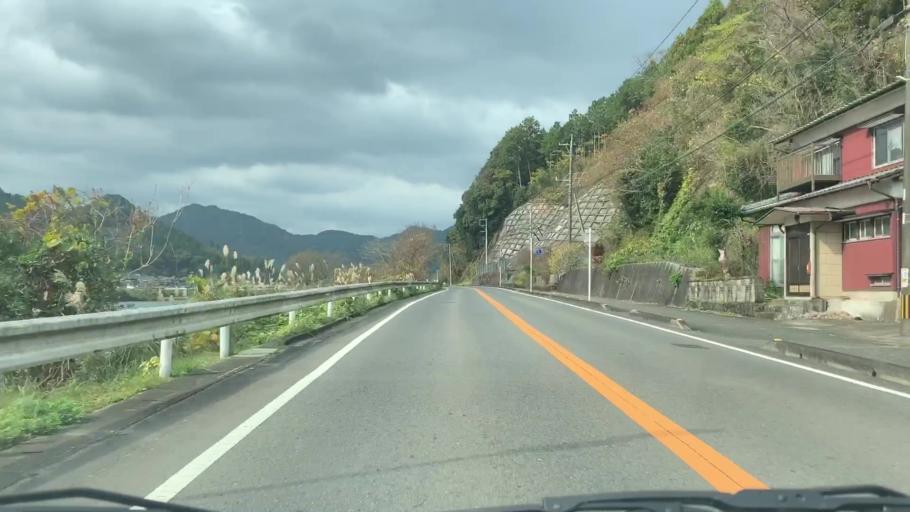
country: JP
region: Saga Prefecture
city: Ureshinomachi-shimojuku
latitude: 33.1281
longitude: 130.0356
